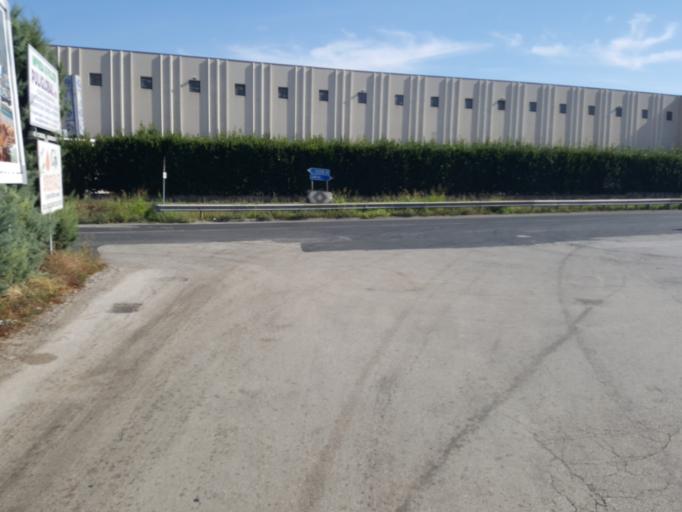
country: IT
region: Campania
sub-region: Provincia di Caserta
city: Pignataro Maggiore
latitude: 41.1640
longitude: 14.1647
